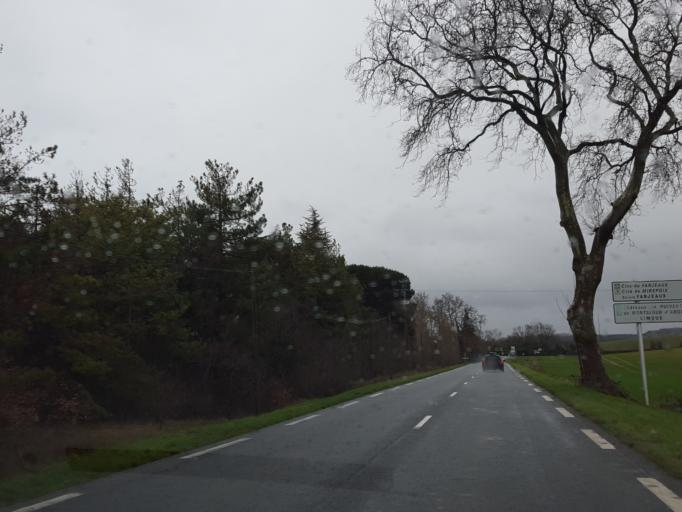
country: FR
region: Languedoc-Roussillon
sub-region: Departement de l'Aude
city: Bram
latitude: 43.1974
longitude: 2.0572
